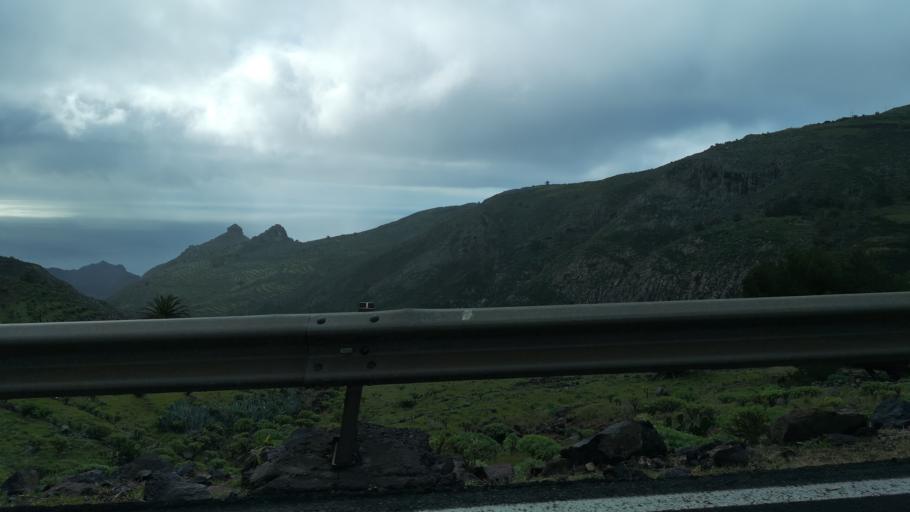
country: ES
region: Canary Islands
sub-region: Provincia de Santa Cruz de Tenerife
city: San Sebastian de la Gomera
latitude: 28.1021
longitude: -17.1695
